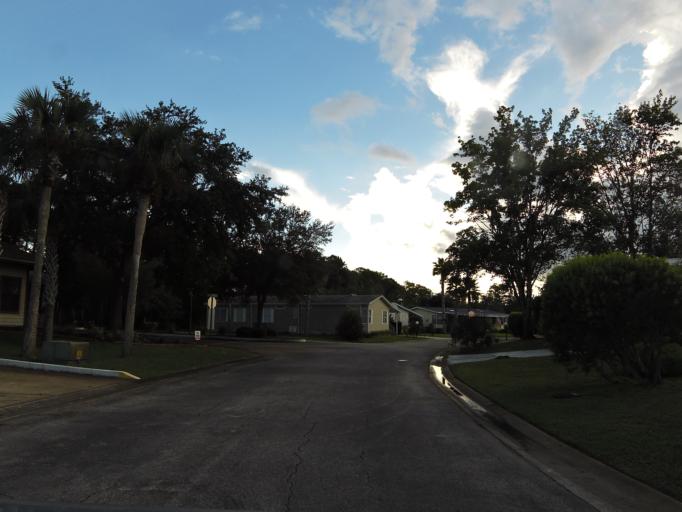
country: US
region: Florida
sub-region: Flagler County
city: Bunnell
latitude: 29.4626
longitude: -81.2617
